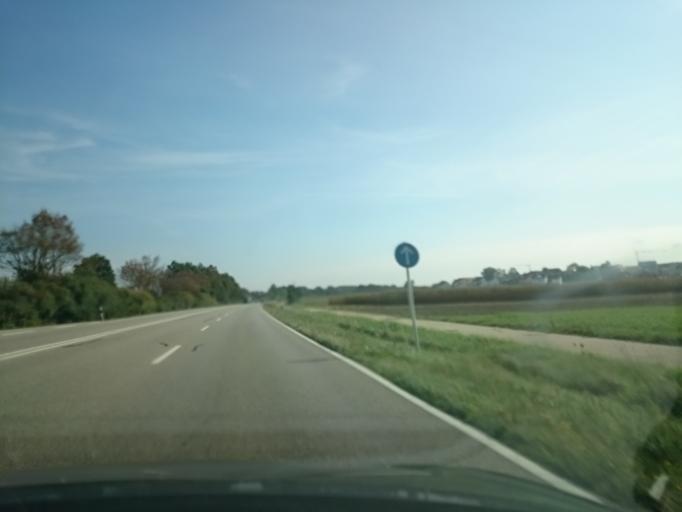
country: DE
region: Bavaria
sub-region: Upper Bavaria
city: Reichertshofen
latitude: 48.6498
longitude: 11.4888
